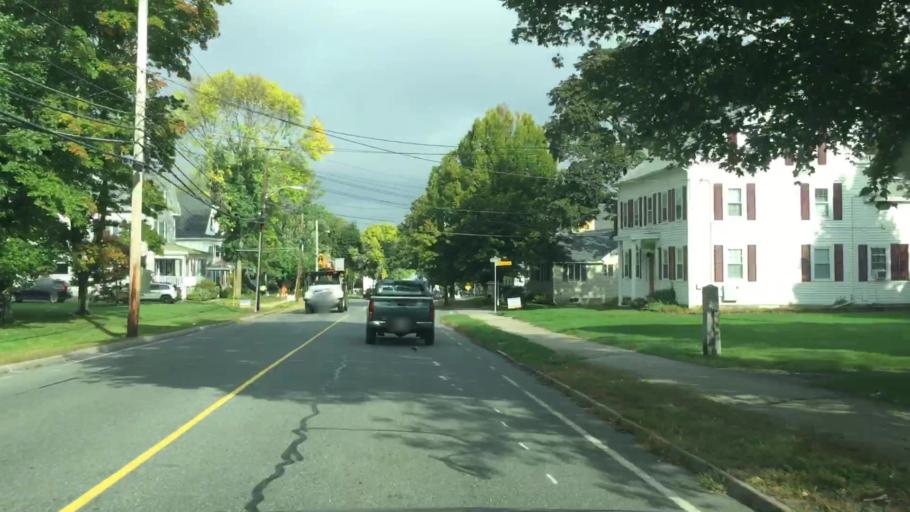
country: US
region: Massachusetts
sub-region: Essex County
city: North Andover
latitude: 42.6988
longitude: -71.1283
